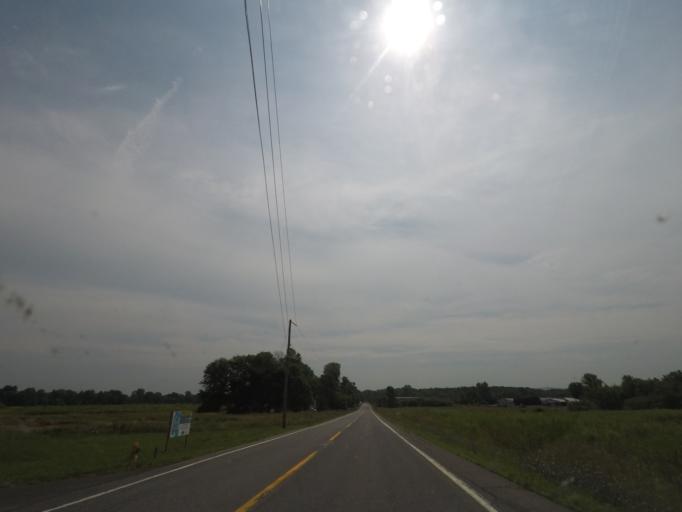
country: US
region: New York
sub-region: Saratoga County
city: Mechanicville
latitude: 42.8874
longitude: -73.7071
